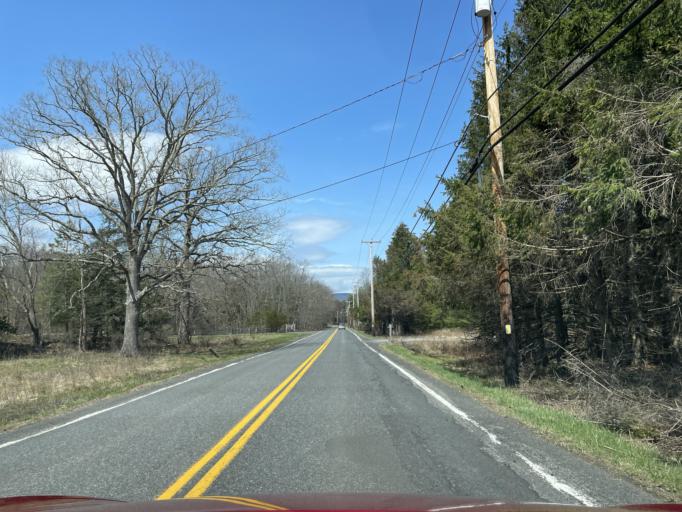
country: US
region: New York
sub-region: Ulster County
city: Manorville
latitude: 42.0934
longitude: -74.0178
